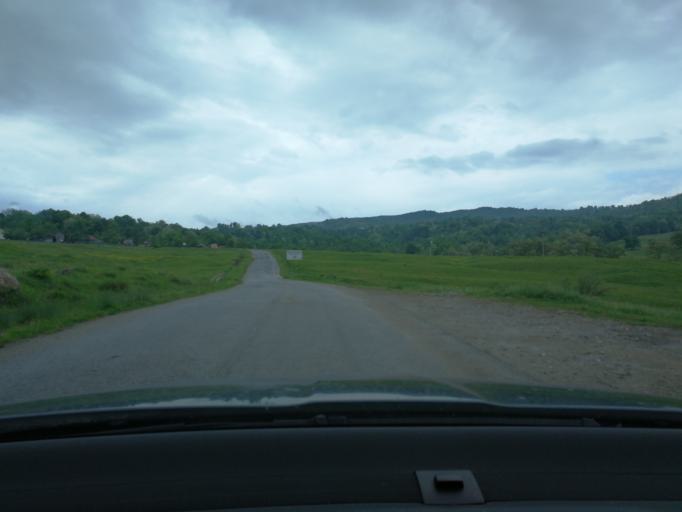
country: RO
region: Prahova
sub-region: Comuna Brebu
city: Pietriceaua
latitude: 45.2069
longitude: 25.8170
